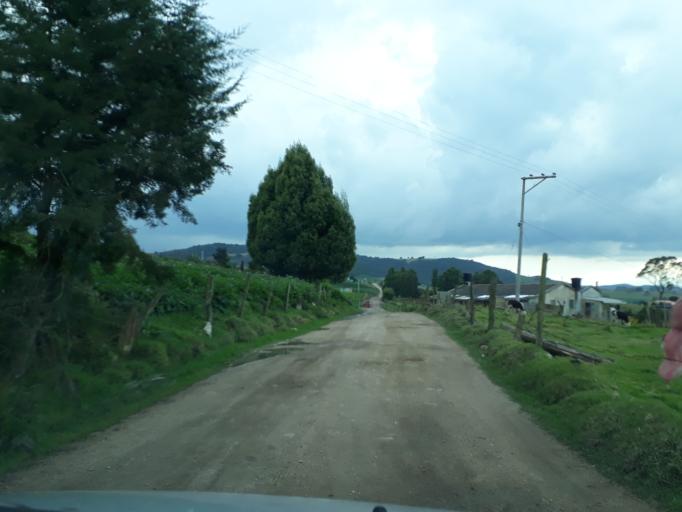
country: CO
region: Cundinamarca
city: Villapinzon
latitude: 5.2410
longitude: -73.6620
